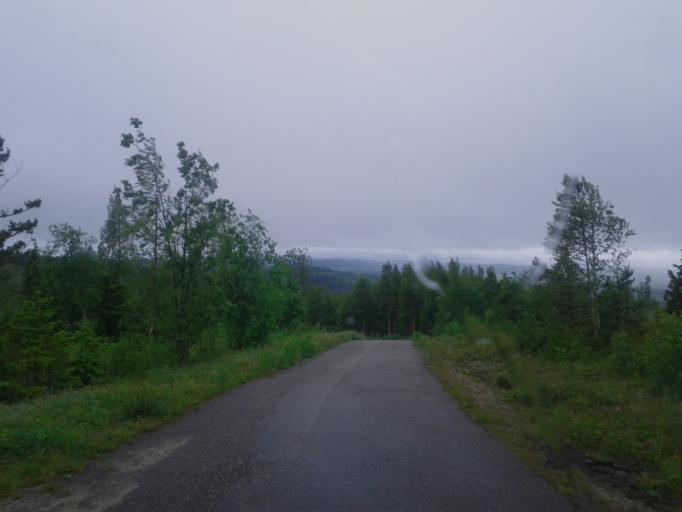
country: SE
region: Vaesternorrland
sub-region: Ange Kommun
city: Fransta
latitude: 62.3861
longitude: 16.3202
